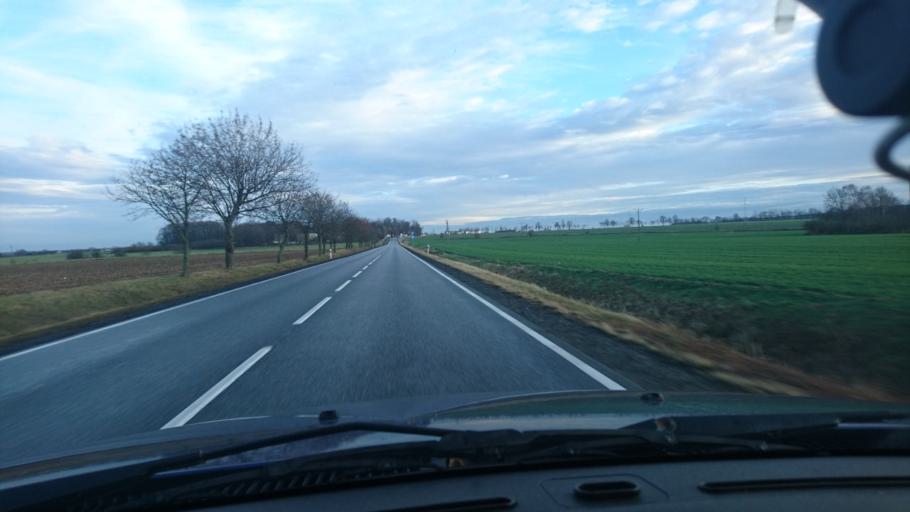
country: PL
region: Greater Poland Voivodeship
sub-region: Powiat kepinski
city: Slupia pod Kepnem
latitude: 51.2442
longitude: 18.0241
